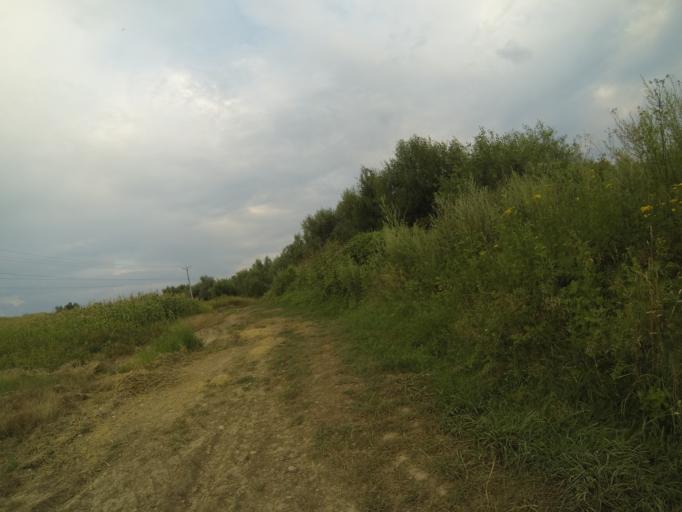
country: RO
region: Brasov
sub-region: Comuna Sinca Veche
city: Sinca Veche
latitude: 45.7734
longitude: 25.1637
